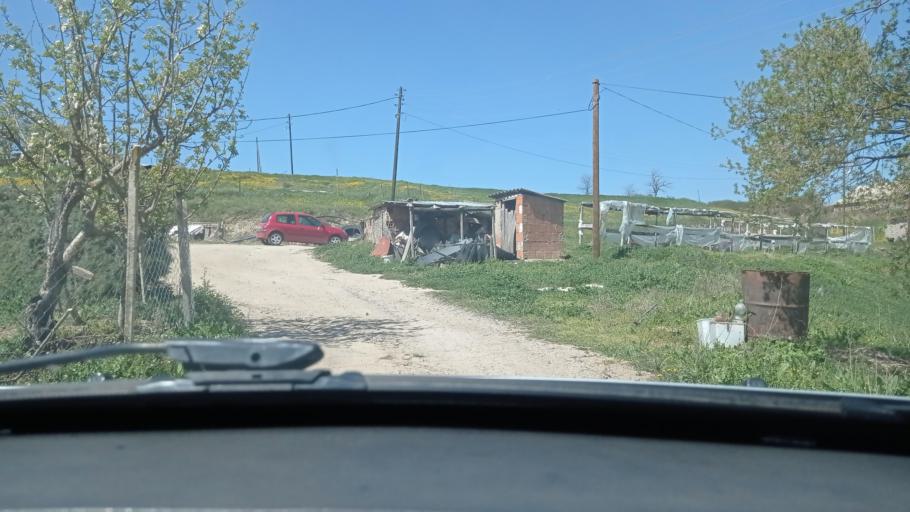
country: MK
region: Lozovo
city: Lozovo
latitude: 41.8042
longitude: 21.8639
